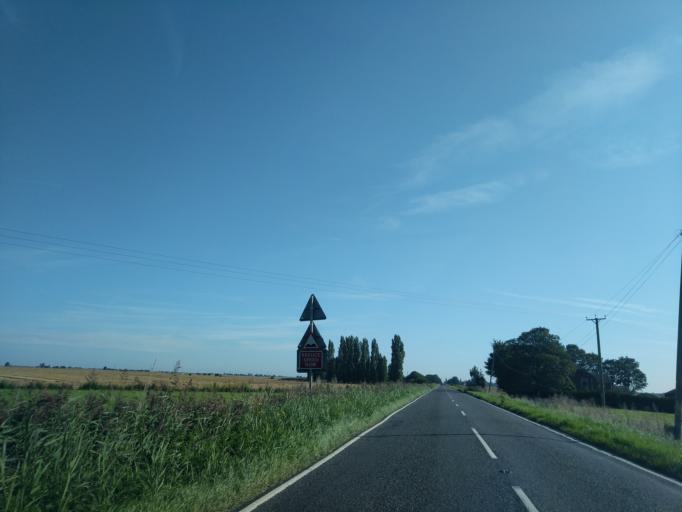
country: GB
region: England
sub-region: Lincolnshire
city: Langtoft
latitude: 52.7730
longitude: -0.2894
